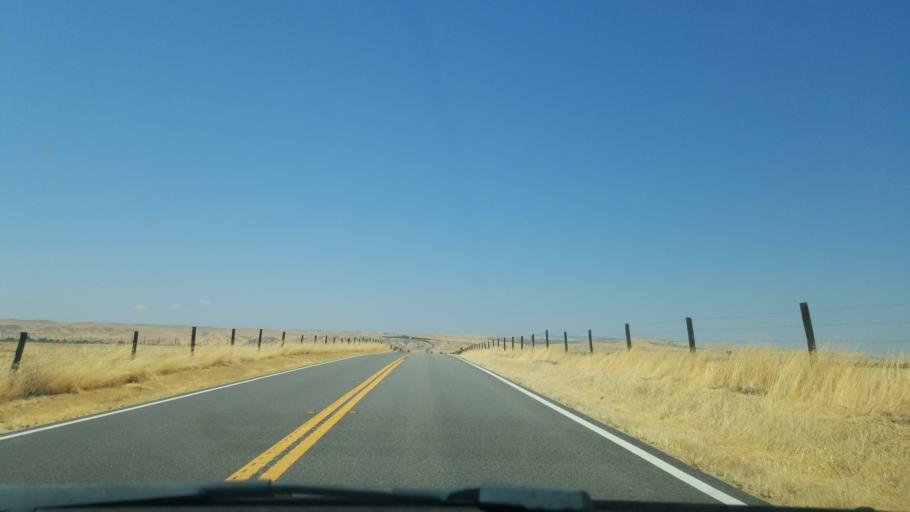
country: US
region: California
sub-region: San Luis Obispo County
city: Shandon
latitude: 35.6233
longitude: -120.3997
